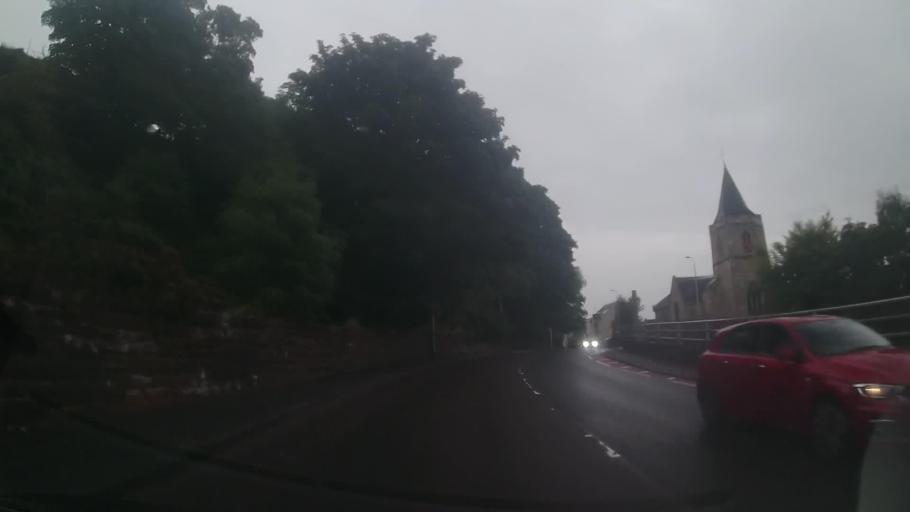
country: GB
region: Scotland
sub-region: North Ayrshire
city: Fairlie
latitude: 55.7612
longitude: -4.8539
